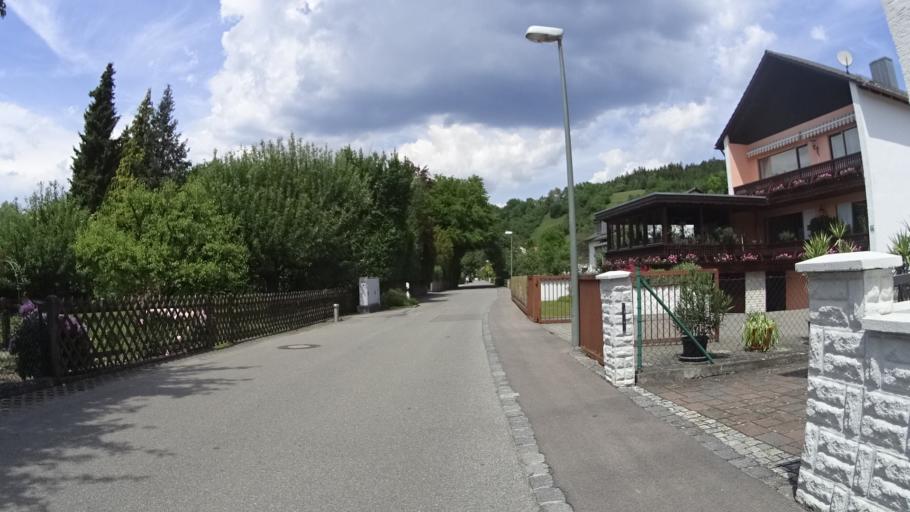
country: DE
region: Bavaria
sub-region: Lower Bavaria
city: Bad Abbach
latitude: 48.9492
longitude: 12.0142
